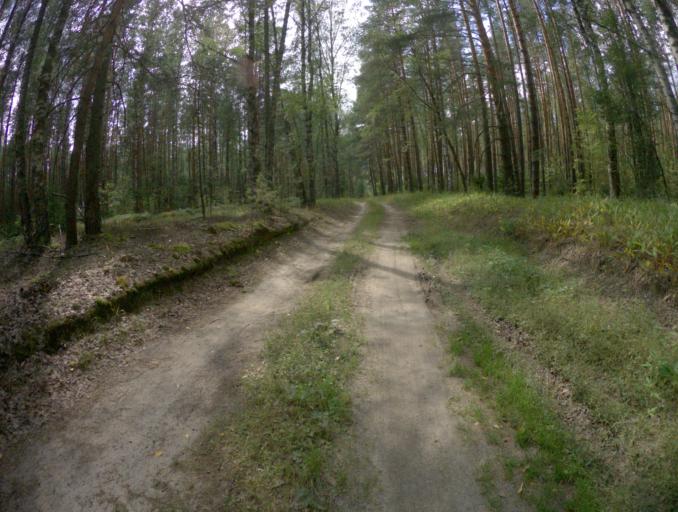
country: RU
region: Vladimir
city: Vorsha
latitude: 55.9666
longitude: 40.1740
